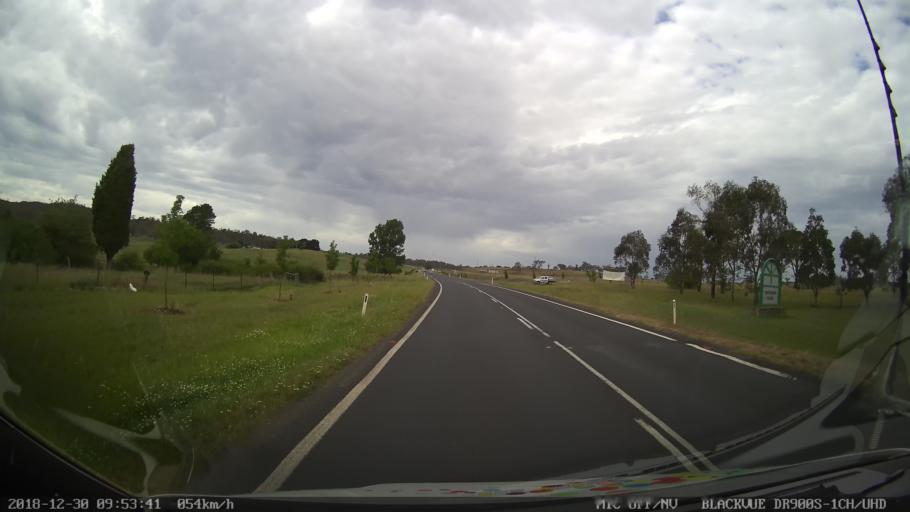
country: AU
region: New South Wales
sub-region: Cooma-Monaro
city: Cooma
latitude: -36.5175
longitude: 149.2813
